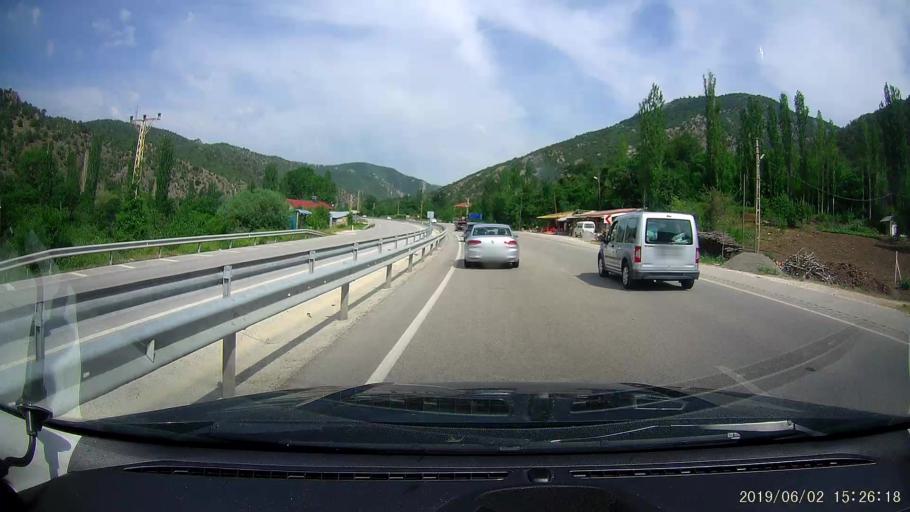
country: TR
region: Amasya
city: Saraycik
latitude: 40.9866
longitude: 35.0337
